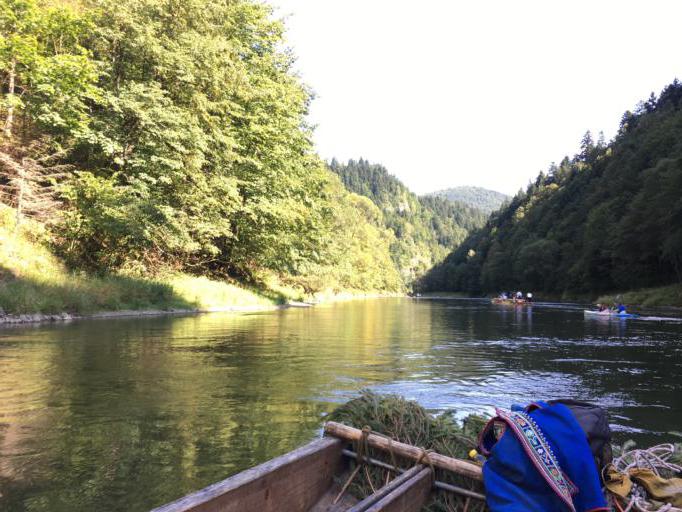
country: PL
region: Lesser Poland Voivodeship
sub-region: Powiat nowotarski
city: Kroscienko nad Dunajcem
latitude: 49.4048
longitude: 20.4217
